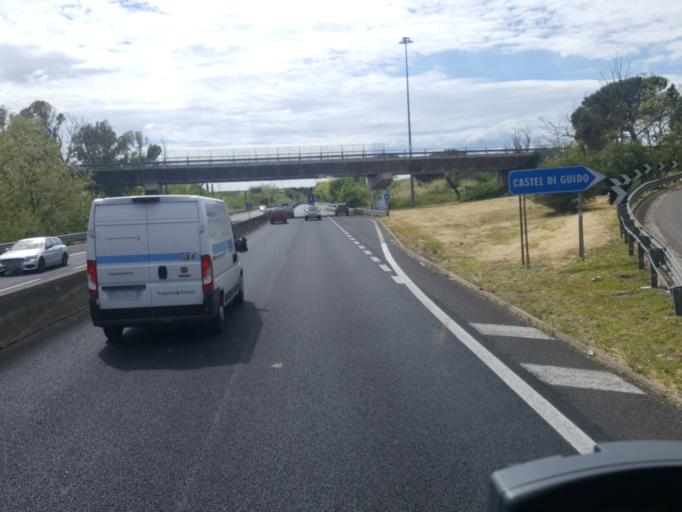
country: IT
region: Latium
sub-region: Citta metropolitana di Roma Capitale
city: La Massimina-Casal Lumbroso
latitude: 41.8857
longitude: 12.3273
